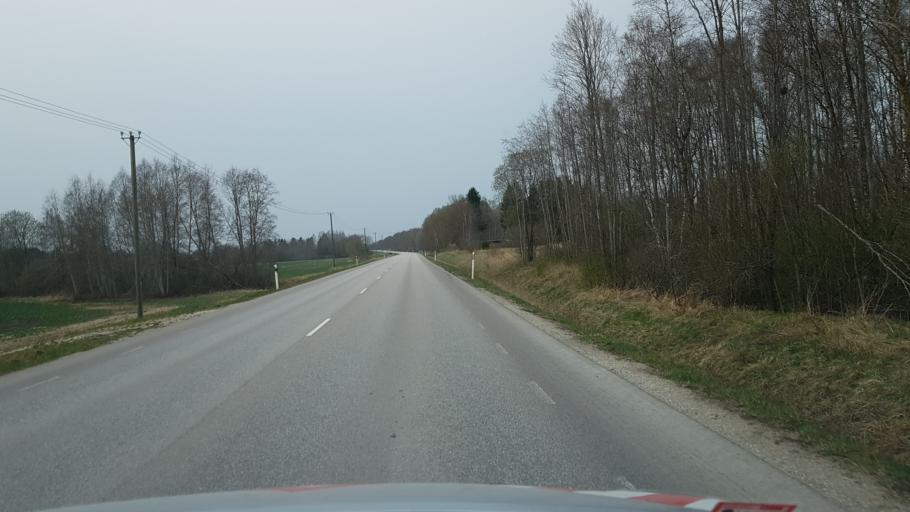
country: EE
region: Harju
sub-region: Joelaehtme vald
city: Loo
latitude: 59.3870
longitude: 24.9925
